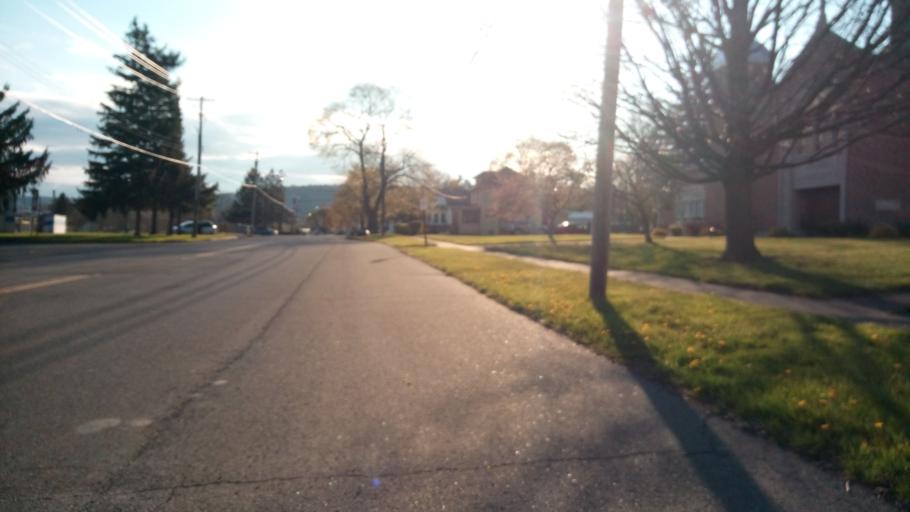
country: US
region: New York
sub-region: Chemung County
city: Elmira Heights
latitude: 42.1224
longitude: -76.8120
